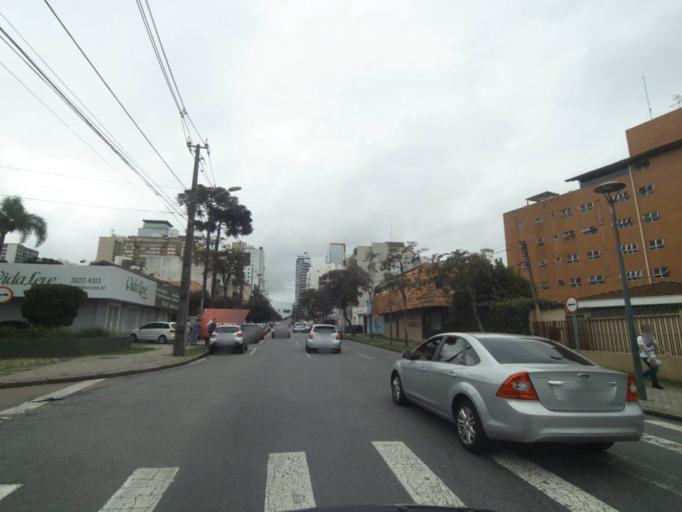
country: BR
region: Parana
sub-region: Curitiba
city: Curitiba
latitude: -25.4186
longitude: -49.2594
